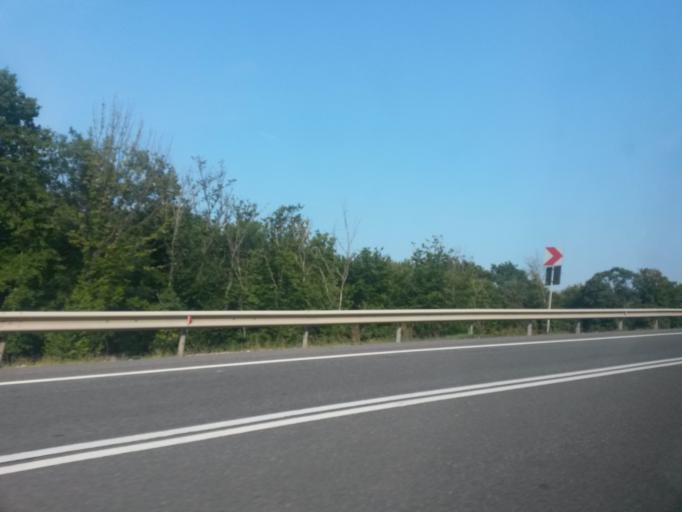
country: RO
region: Cluj
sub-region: Comuna Feleacu
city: Gheorghieni
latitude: 46.7184
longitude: 23.6600
